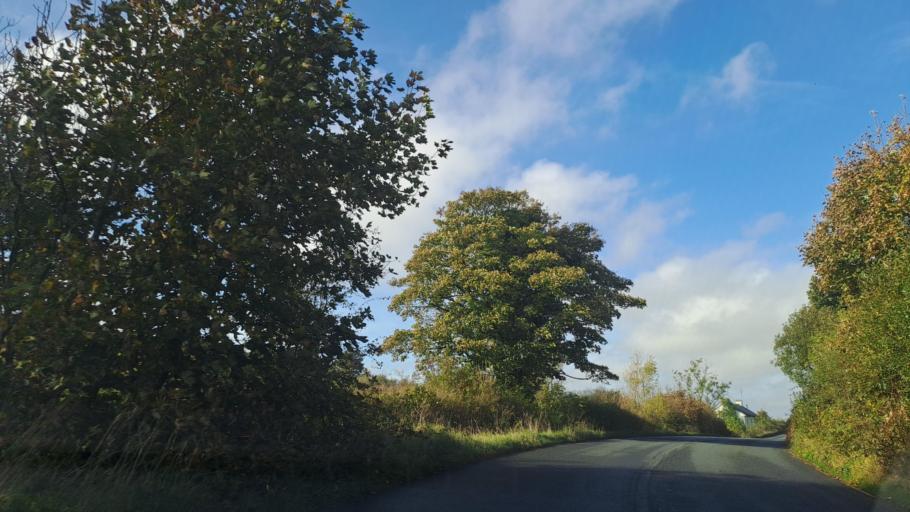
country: IE
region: Ulster
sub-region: An Cabhan
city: Bailieborough
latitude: 54.0229
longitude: -6.9510
